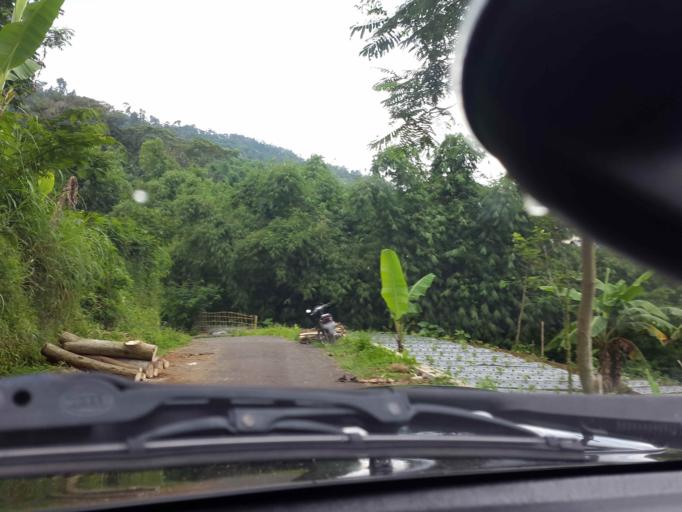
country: ID
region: Central Java
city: Wonosobo
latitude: -7.3583
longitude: 109.9593
